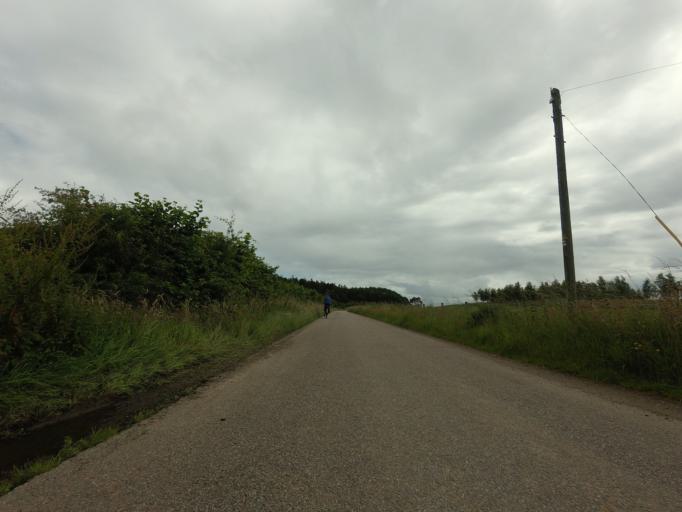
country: GB
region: Scotland
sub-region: Moray
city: Lhanbryd
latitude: 57.6671
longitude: -3.1694
